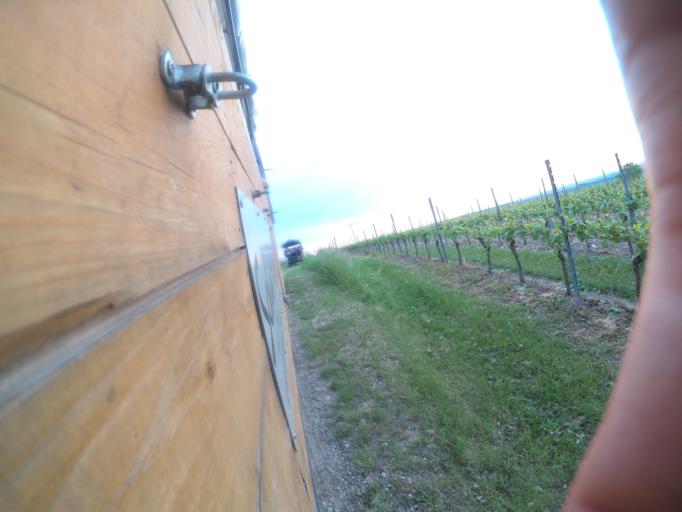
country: DE
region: Rheinland-Pfalz
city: Dalheim
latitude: 49.8236
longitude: 8.2939
